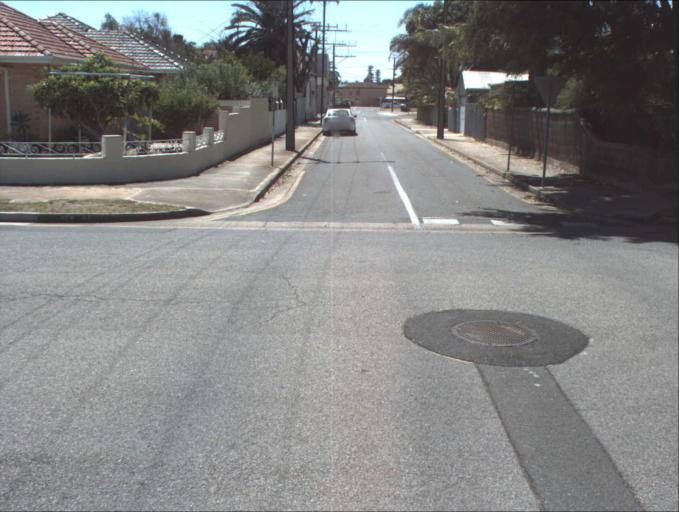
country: AU
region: South Australia
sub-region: Port Adelaide Enfield
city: Cheltenham
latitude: -34.8570
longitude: 138.5092
